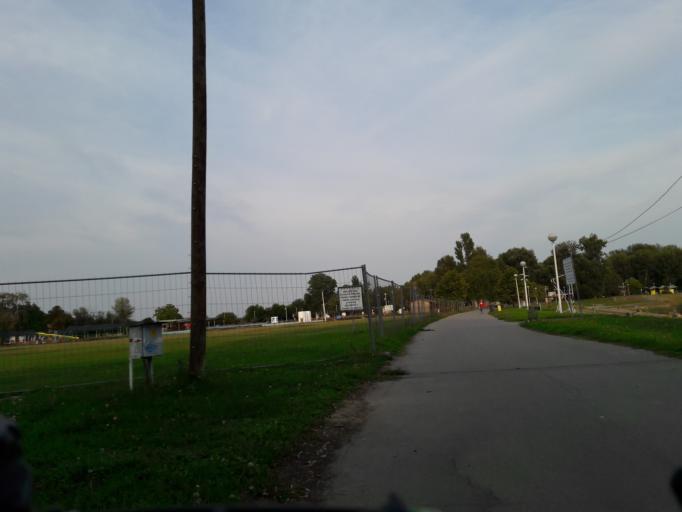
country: HR
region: Osjecko-Baranjska
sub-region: Grad Osijek
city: Osijek
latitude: 45.5655
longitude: 18.6931
